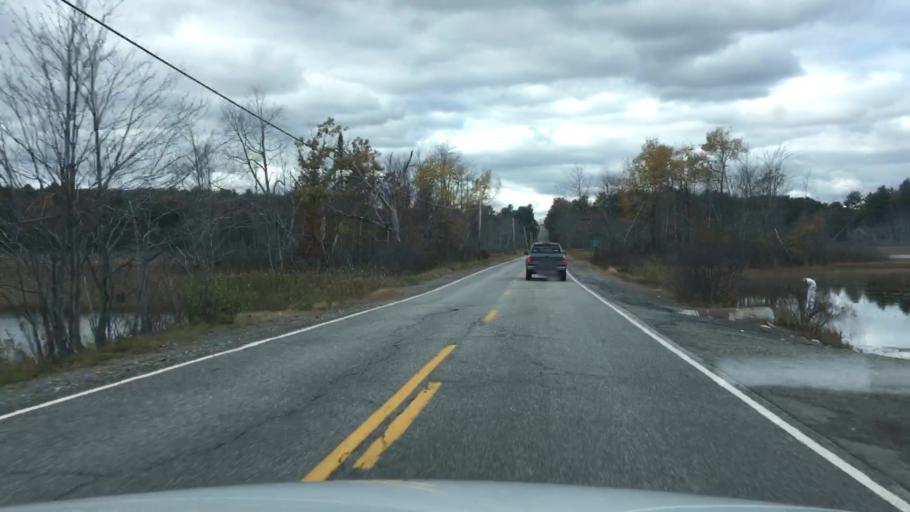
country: US
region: Maine
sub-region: Sagadahoc County
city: Richmond
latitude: 44.1062
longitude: -69.8980
